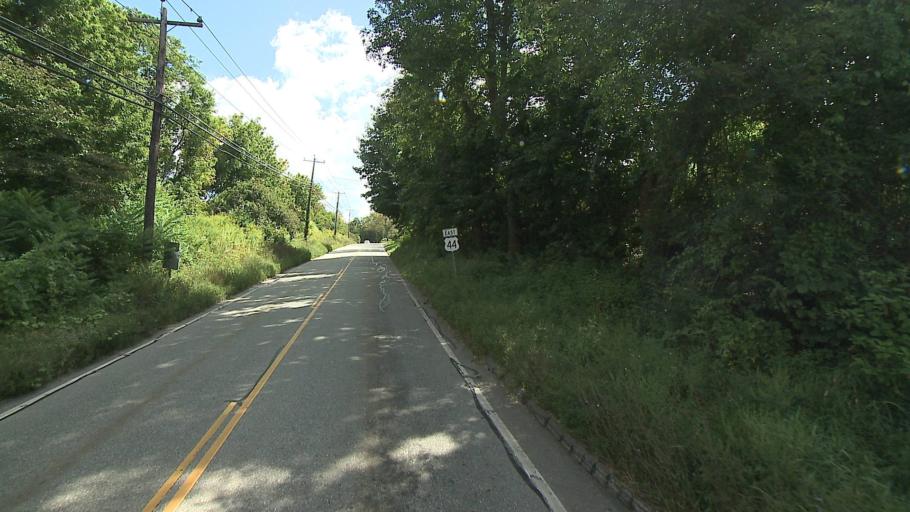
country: US
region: Connecticut
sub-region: Windham County
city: Putnam
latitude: 41.8973
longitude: -71.9367
